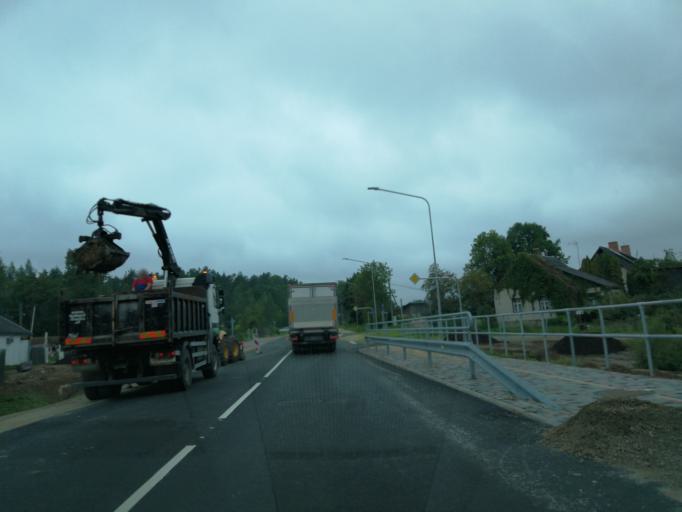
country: LV
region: Livani
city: Livani
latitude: 56.3568
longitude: 26.1864
